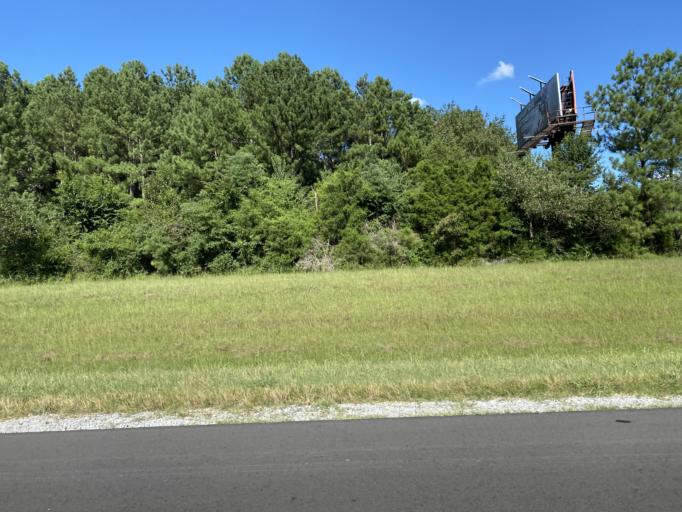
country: US
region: Alabama
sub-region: Limestone County
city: Athens
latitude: 34.7598
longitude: -86.9384
